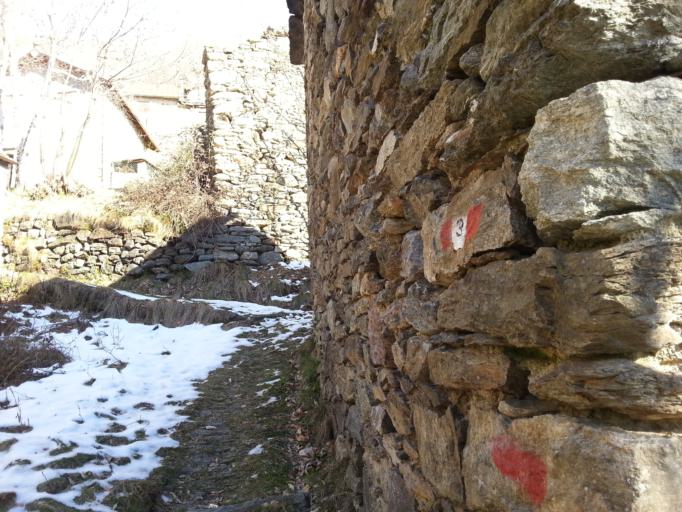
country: IT
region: Lombardy
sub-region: Provincia di Como
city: Plesio
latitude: 46.0638
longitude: 9.2414
